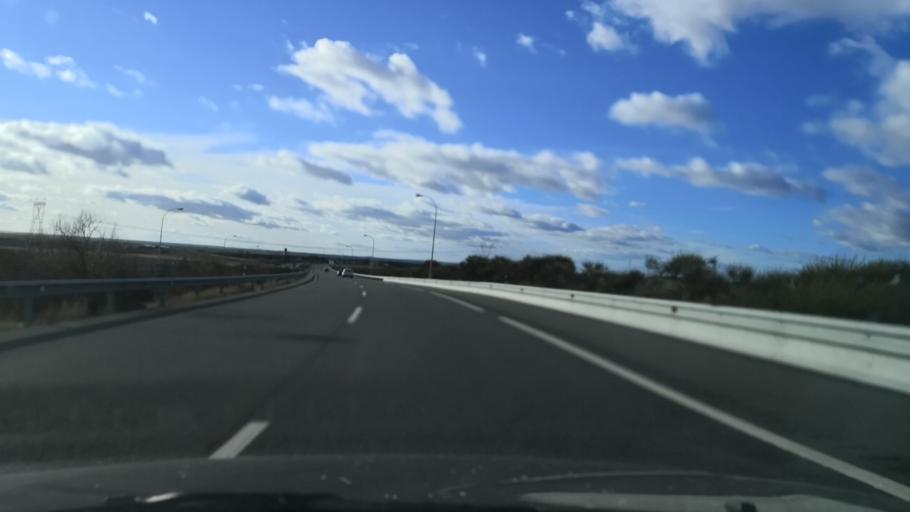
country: ES
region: Castille and Leon
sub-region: Provincia de Avila
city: Adanero
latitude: 40.9491
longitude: -4.5950
